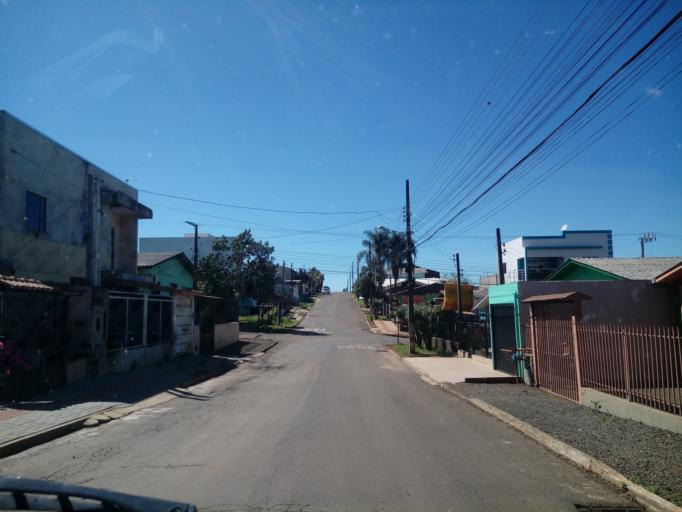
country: BR
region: Santa Catarina
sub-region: Chapeco
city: Chapeco
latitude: -27.0890
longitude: -52.6745
